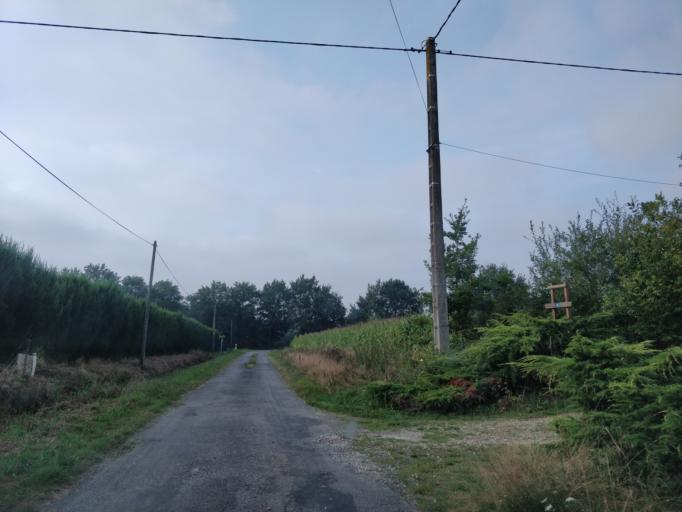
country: FR
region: Brittany
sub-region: Departement d'Ille-et-Vilaine
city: Noyal-sur-Vilaine
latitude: 48.1030
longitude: -1.5511
